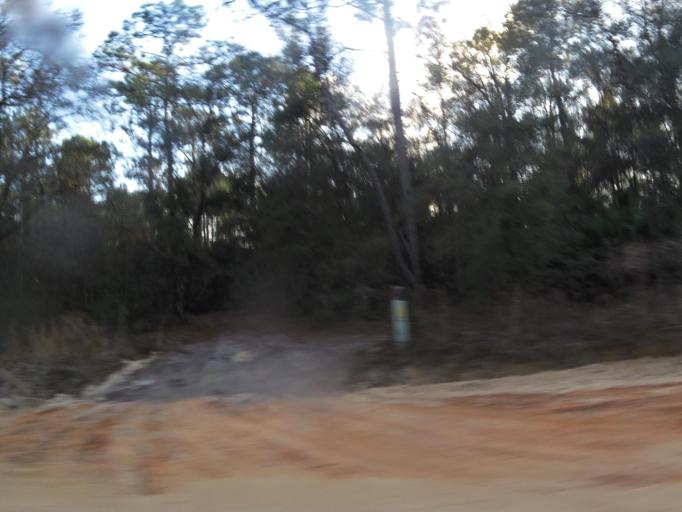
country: US
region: Florida
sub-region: Putnam County
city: Interlachen
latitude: 29.7835
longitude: -81.8637
